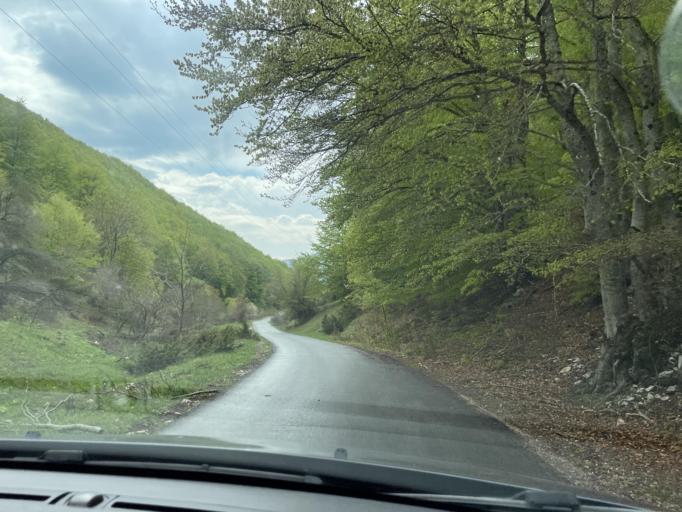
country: MK
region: Opstina Rostusa
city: Rostusha
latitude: 41.5939
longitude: 20.6698
